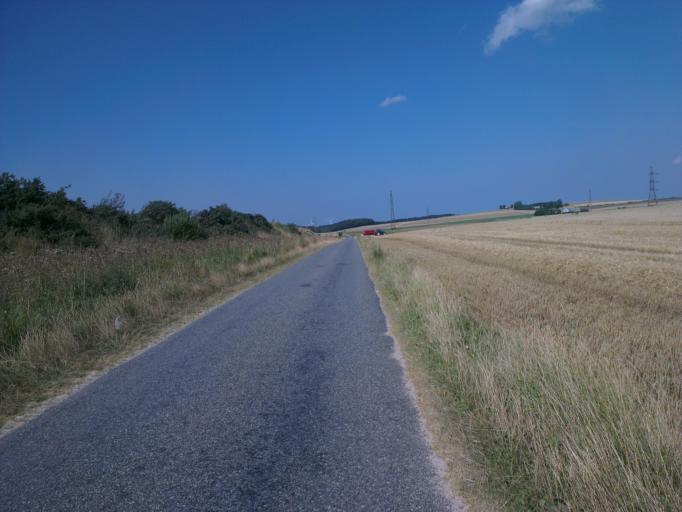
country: DK
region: Capital Region
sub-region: Frederikssund Kommune
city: Skibby
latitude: 55.8011
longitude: 11.9096
